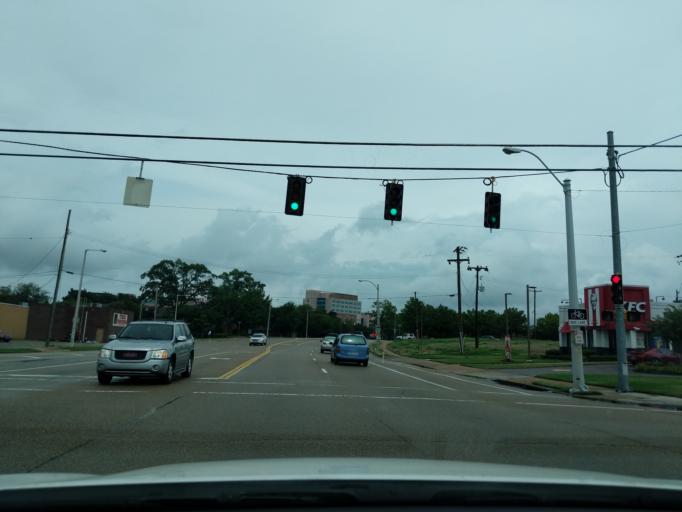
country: US
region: Tennessee
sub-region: Shelby County
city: Memphis
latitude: 35.1482
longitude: -90.0436
